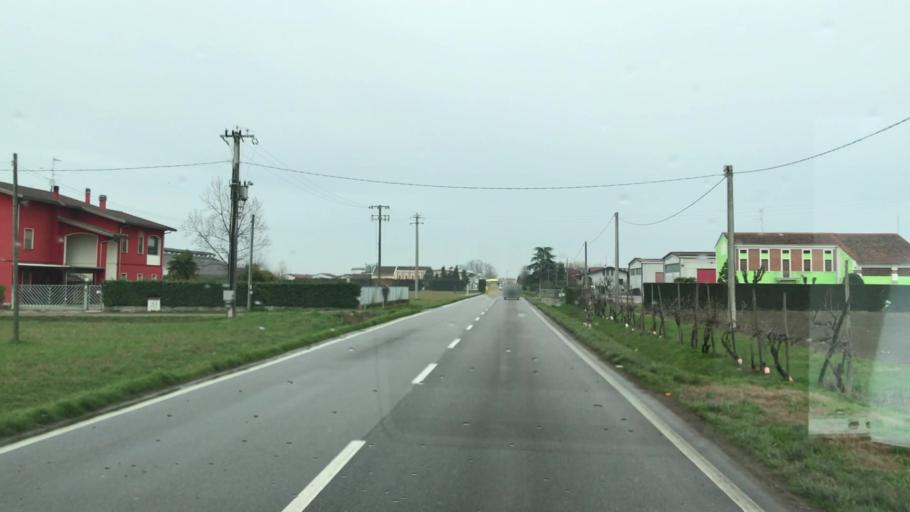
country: IT
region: Lombardy
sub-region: Provincia di Mantova
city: Commessaggio
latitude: 44.9874
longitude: 10.5733
